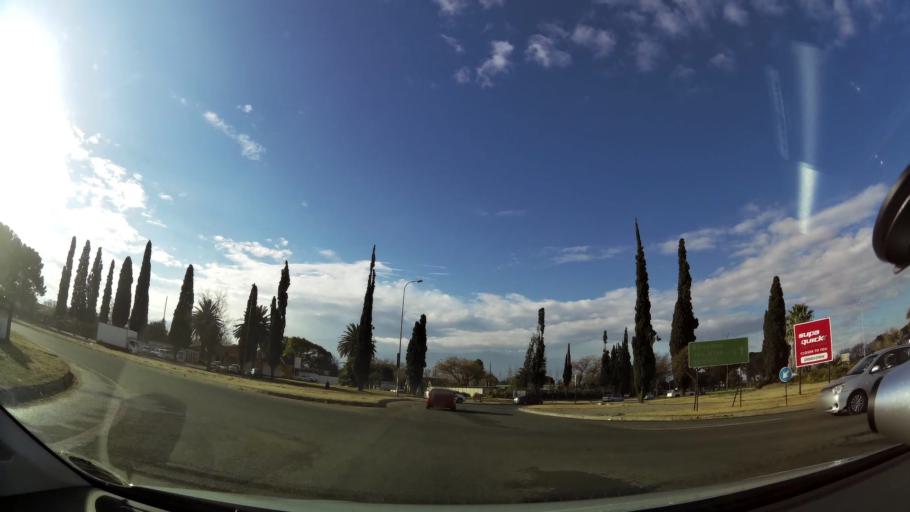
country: ZA
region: Orange Free State
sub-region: Lejweleputswa District Municipality
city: Welkom
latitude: -27.9873
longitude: 26.7554
